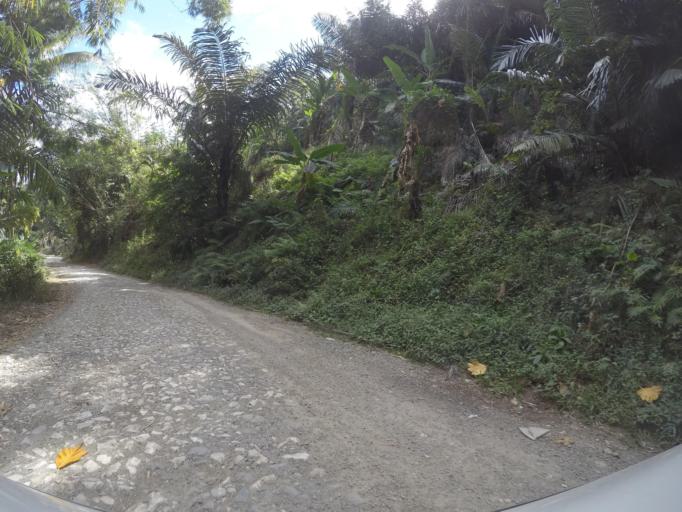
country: TL
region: Baucau
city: Baucau
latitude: -8.6191
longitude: 126.6598
